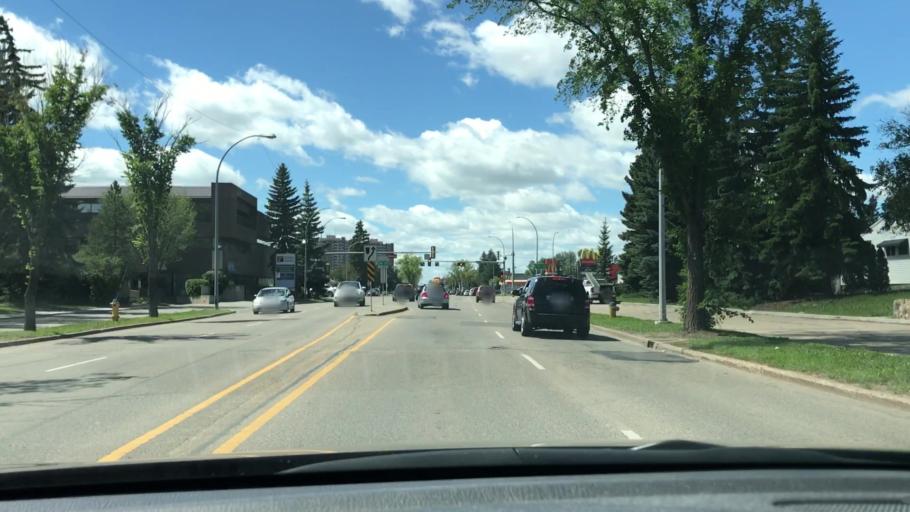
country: CA
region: Alberta
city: Edmonton
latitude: 53.5194
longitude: -113.5760
